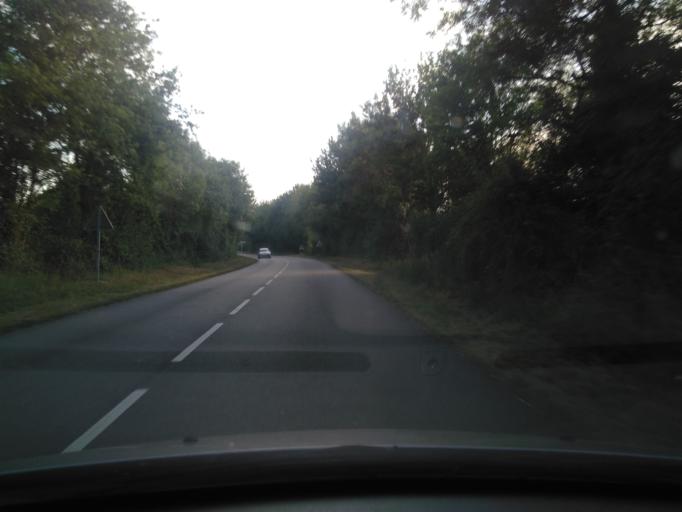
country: FR
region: Pays de la Loire
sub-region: Departement de la Vendee
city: Nesmy
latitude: 46.6190
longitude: -1.4098
